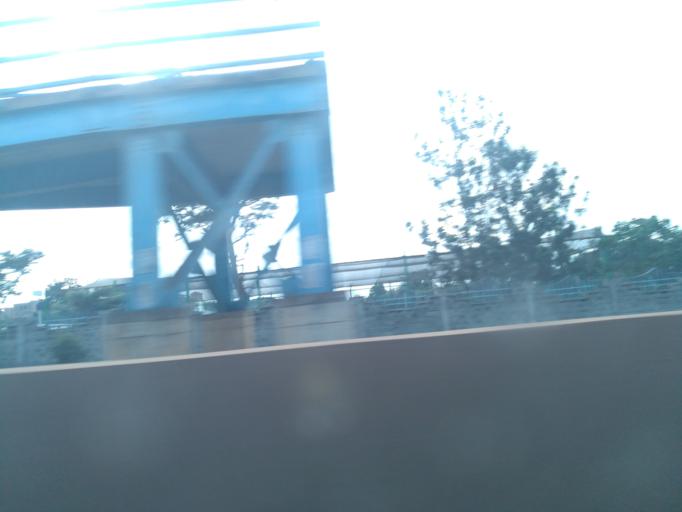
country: KE
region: Nairobi Area
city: Thika
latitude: -1.1213
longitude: 37.0072
